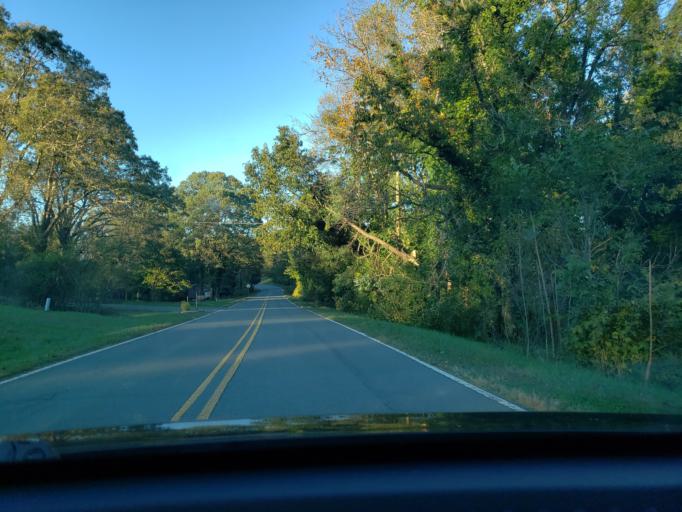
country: US
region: North Carolina
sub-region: Forsyth County
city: Walkertown
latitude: 36.2259
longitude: -80.1988
